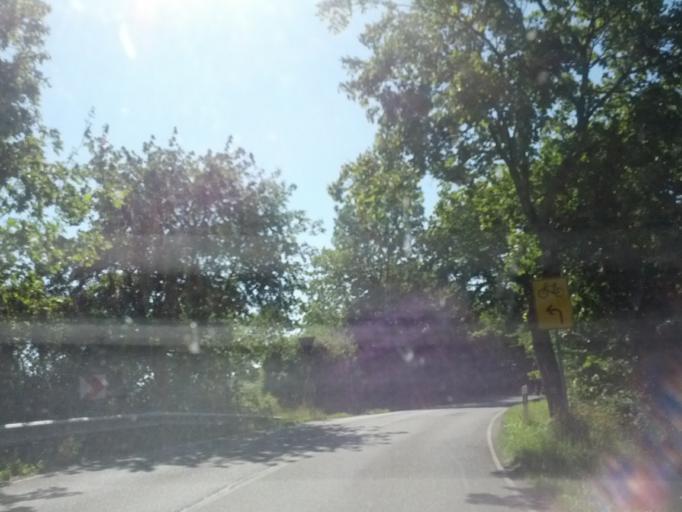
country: DE
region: Mecklenburg-Vorpommern
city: Bergen auf Ruegen
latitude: 54.4384
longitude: 13.4366
